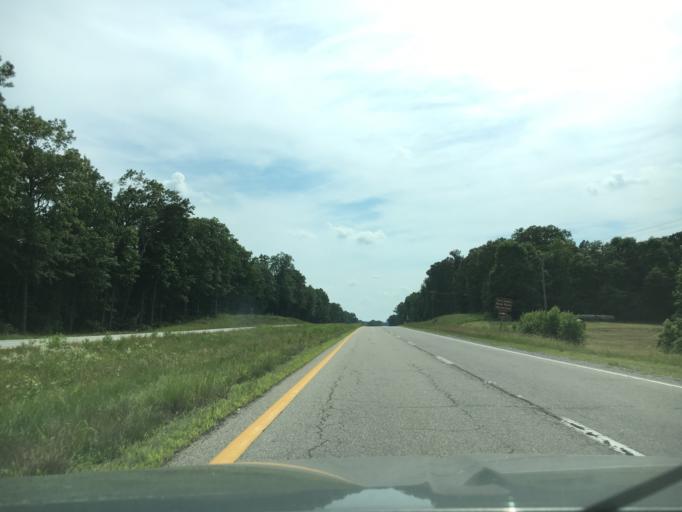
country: US
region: Virginia
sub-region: Nottoway County
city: Crewe
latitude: 37.1533
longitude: -78.2802
